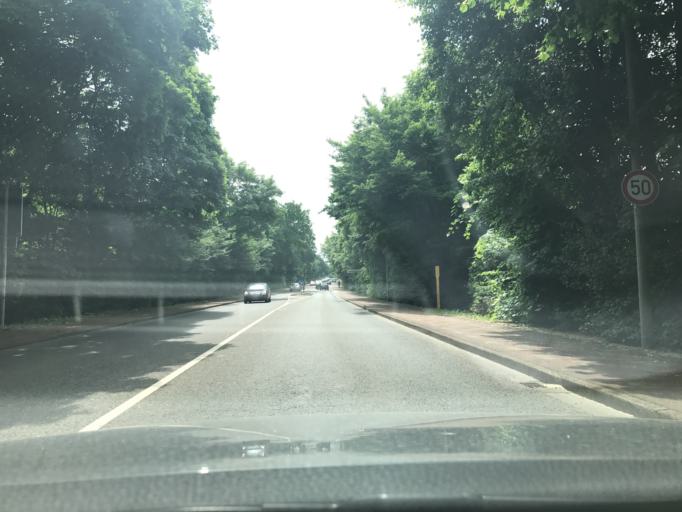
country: DE
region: North Rhine-Westphalia
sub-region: Regierungsbezirk Dusseldorf
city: Krefeld
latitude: 51.3505
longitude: 6.6377
